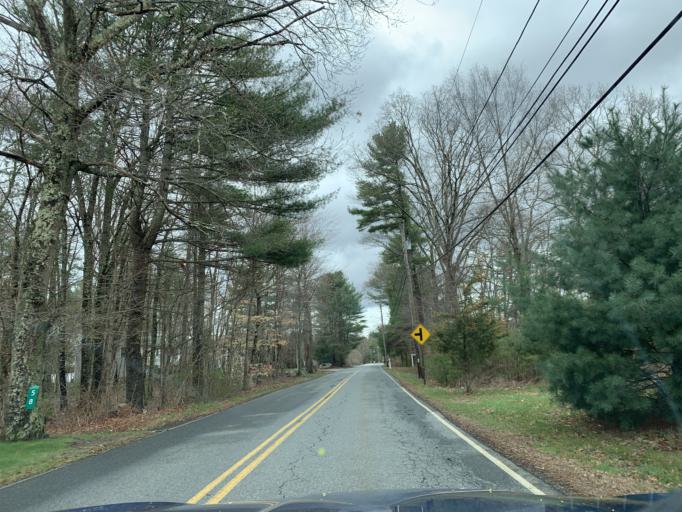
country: US
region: Massachusetts
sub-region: Bristol County
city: Norton
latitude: 41.9391
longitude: -71.2205
